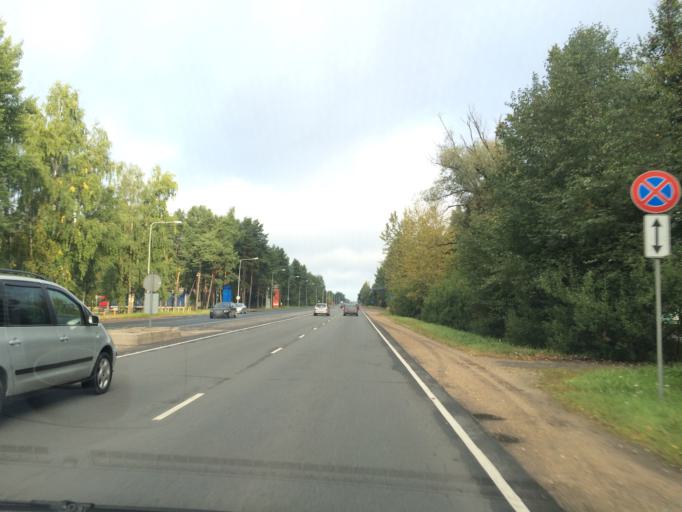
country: LV
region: Kekava
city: Kekava
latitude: 56.8824
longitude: 24.2455
